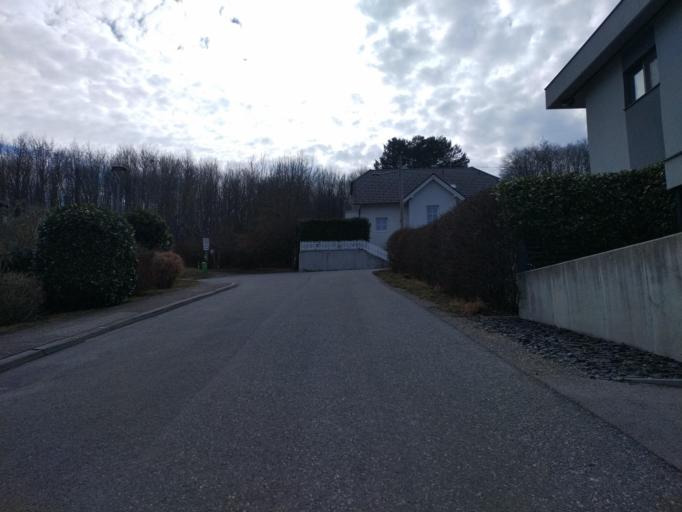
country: AT
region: Lower Austria
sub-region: Politischer Bezirk Wien-Umgebung
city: Mauerbach
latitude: 48.2436
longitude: 16.1614
